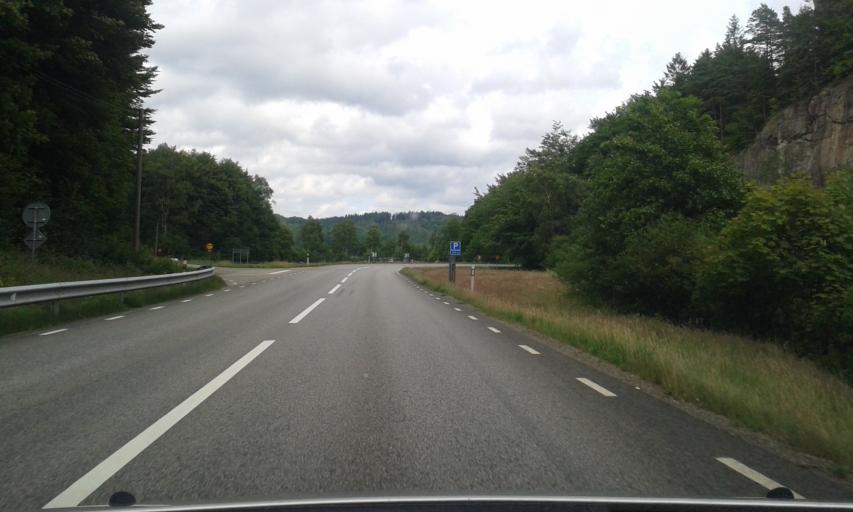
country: SE
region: Halland
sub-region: Varbergs Kommun
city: Tvaaker
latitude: 57.1519
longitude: 12.5857
